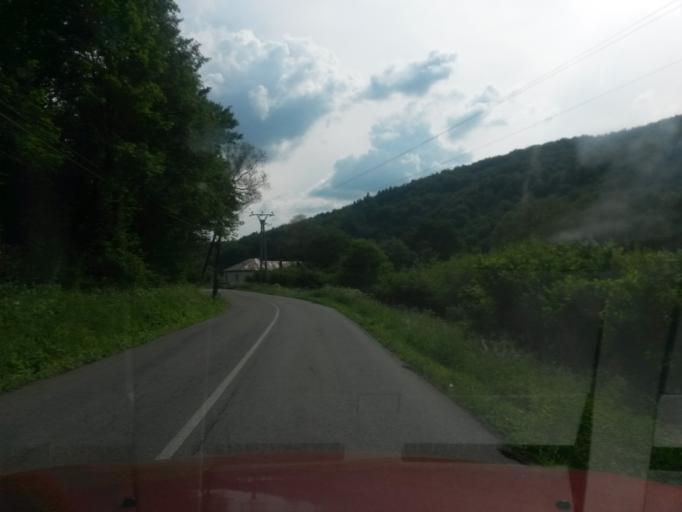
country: SK
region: Presovsky
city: Snina
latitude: 49.1192
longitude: 22.0752
